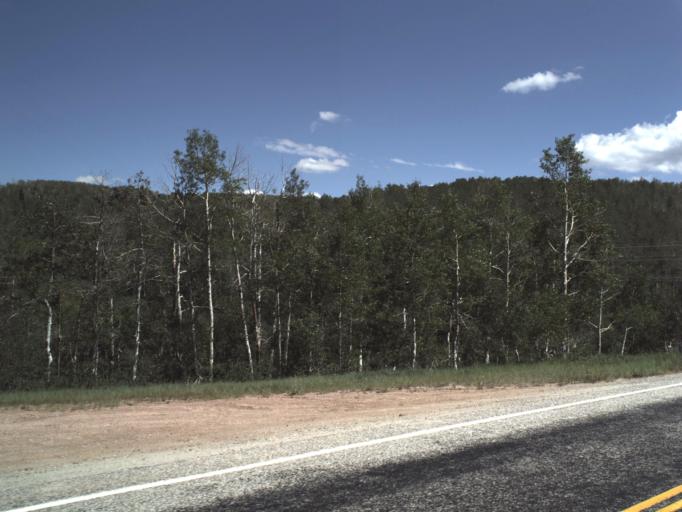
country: US
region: Utah
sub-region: Weber County
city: Wolf Creek
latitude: 41.4098
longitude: -111.5399
